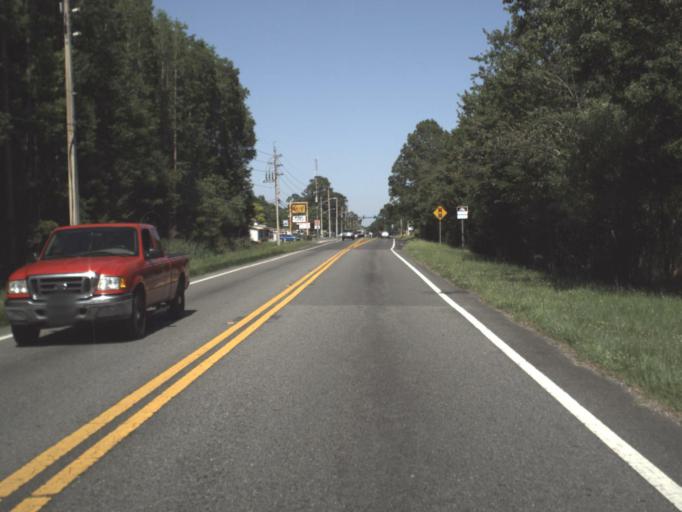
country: US
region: Florida
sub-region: Duval County
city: Jacksonville
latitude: 30.3186
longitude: -81.8097
